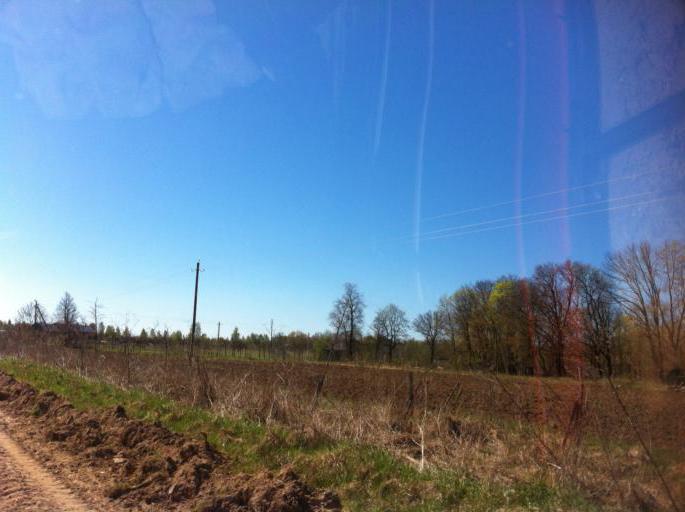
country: RU
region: Pskov
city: Izborsk
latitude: 57.8110
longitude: 27.9795
